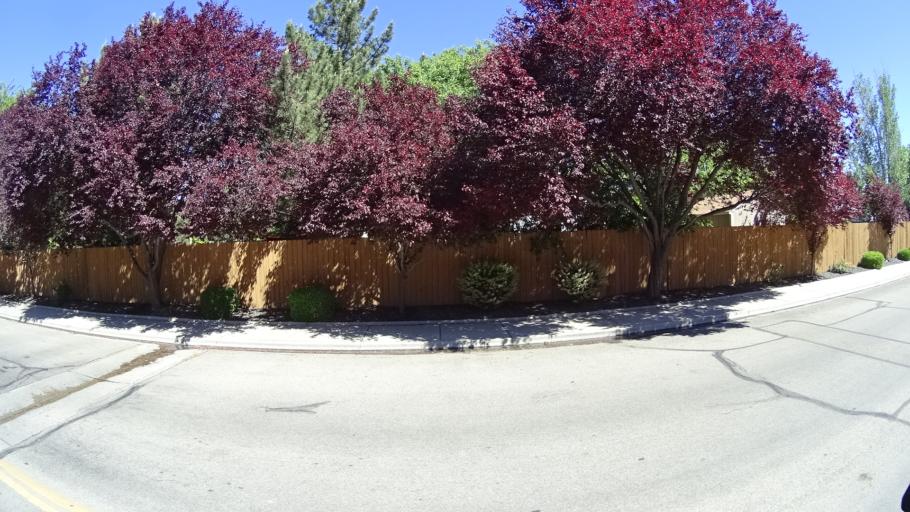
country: US
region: Idaho
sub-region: Ada County
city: Meridian
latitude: 43.6249
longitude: -116.3740
